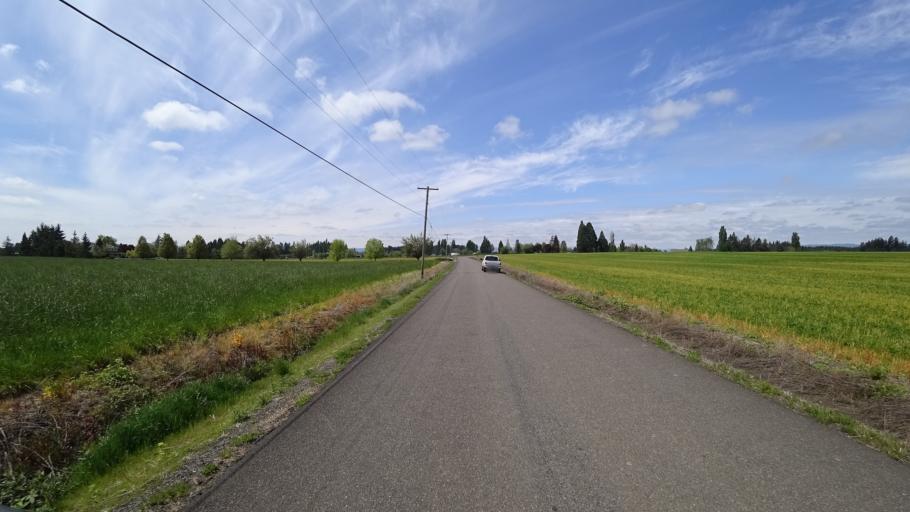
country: US
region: Oregon
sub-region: Washington County
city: North Plains
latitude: 45.5660
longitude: -122.9454
